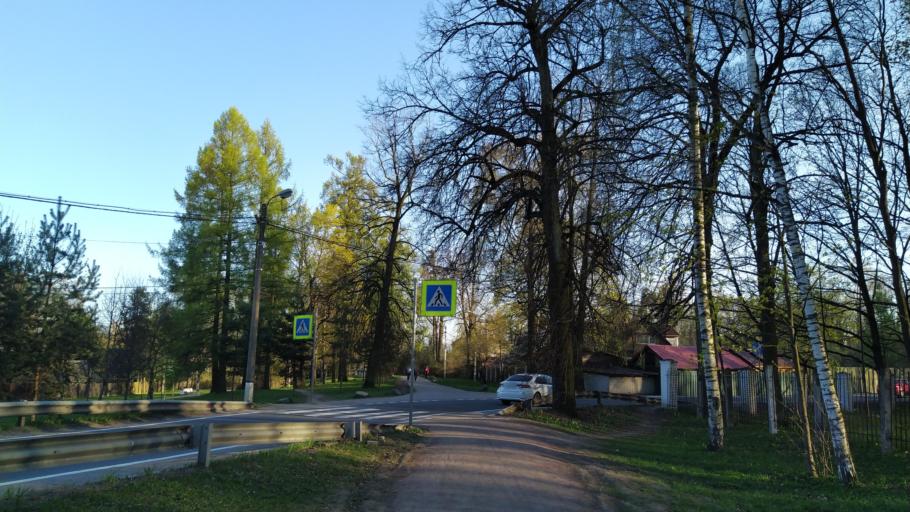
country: RU
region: St.-Petersburg
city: Pavlovsk
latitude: 59.6972
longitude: 30.4289
